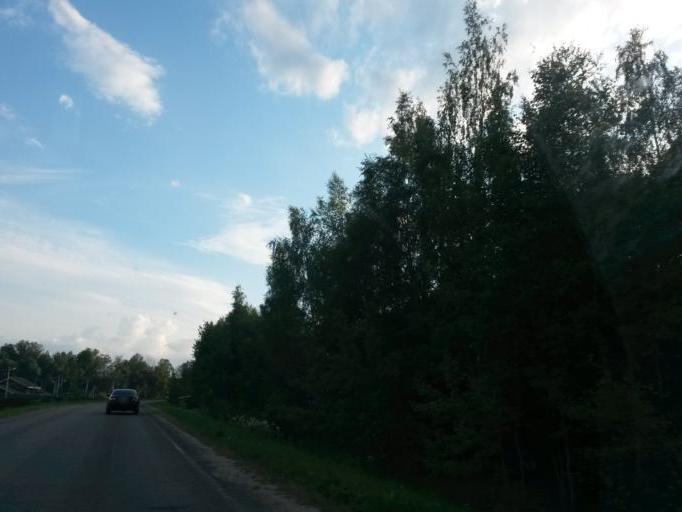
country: RU
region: Moskovskaya
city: Barybino
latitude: 55.2500
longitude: 37.8171
